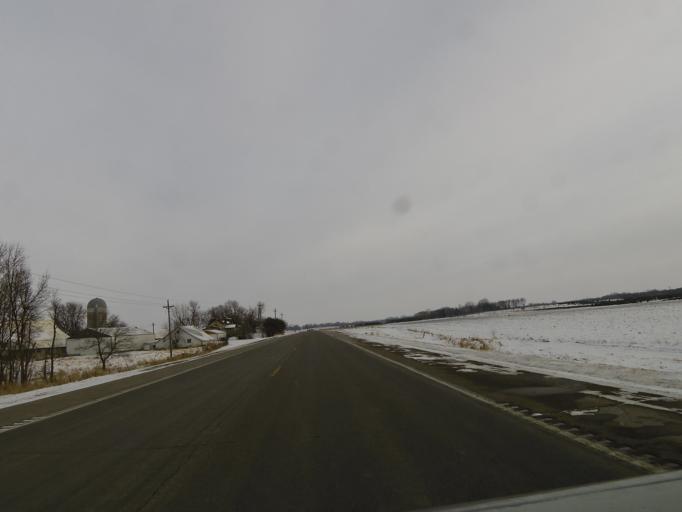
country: US
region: Minnesota
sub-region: McLeod County
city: Lester Prairie
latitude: 44.9061
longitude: -94.0014
